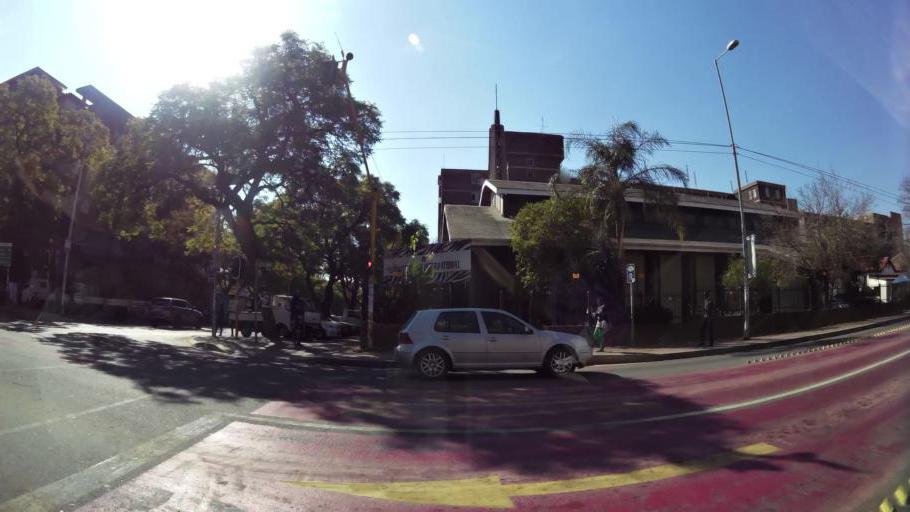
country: ZA
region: Gauteng
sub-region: City of Tshwane Metropolitan Municipality
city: Pretoria
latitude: -25.7543
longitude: 28.2059
